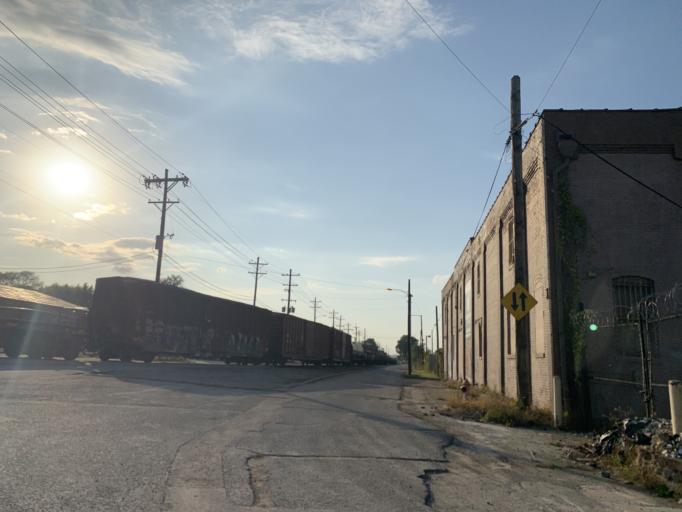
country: US
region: Kentucky
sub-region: Jefferson County
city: Louisville
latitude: 38.2299
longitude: -85.7684
